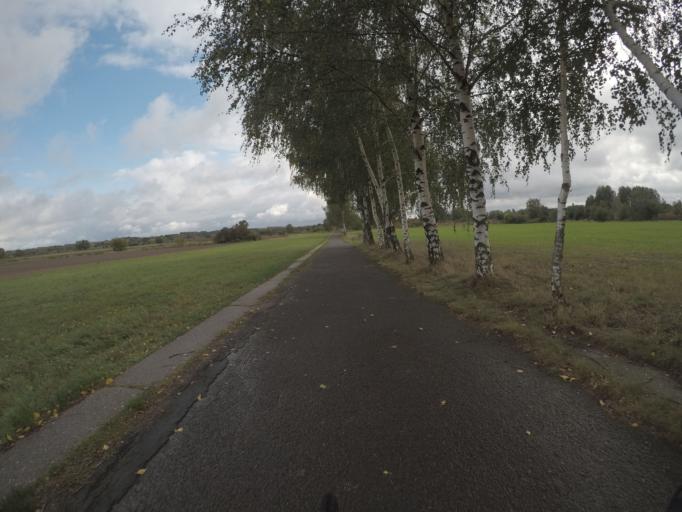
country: DE
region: Berlin
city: Rosenthal
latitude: 52.6131
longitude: 13.3773
